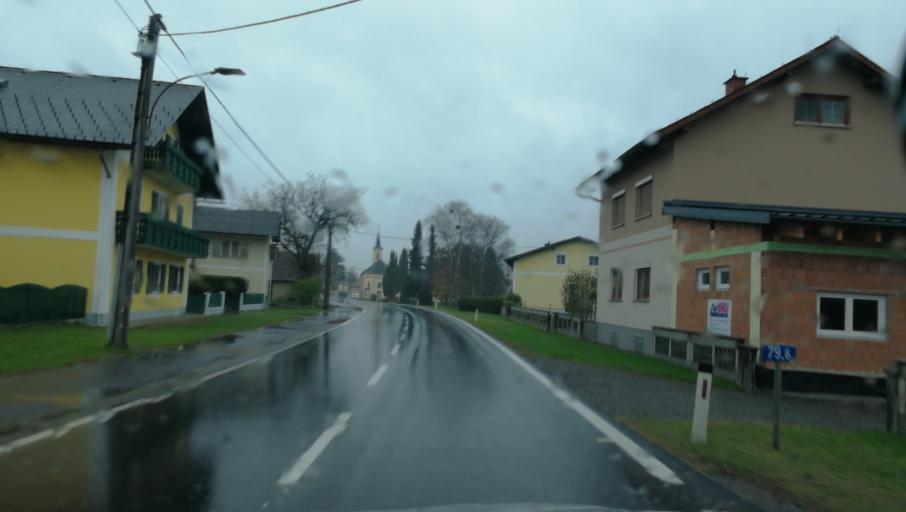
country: SI
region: Sentilj
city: Selnica ob Muri
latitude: 46.7119
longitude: 15.6938
